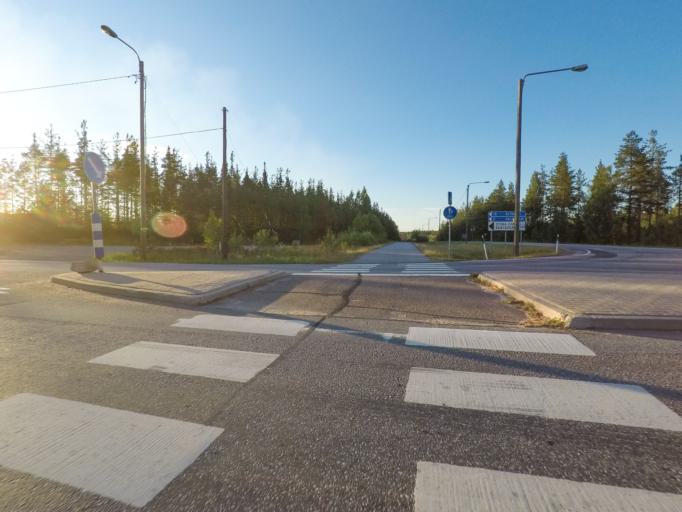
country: FI
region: South Karelia
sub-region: Imatra
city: Ruokolahti
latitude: 61.2561
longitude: 28.8787
